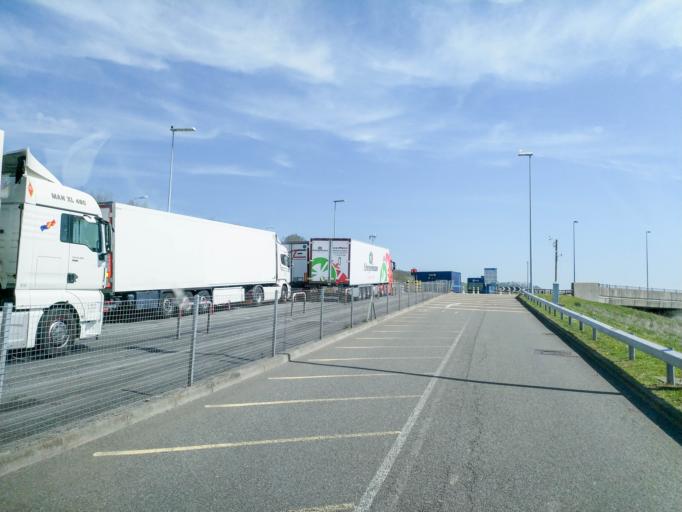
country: GB
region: England
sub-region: Kent
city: Hawkinge
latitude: 51.0975
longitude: 1.1316
